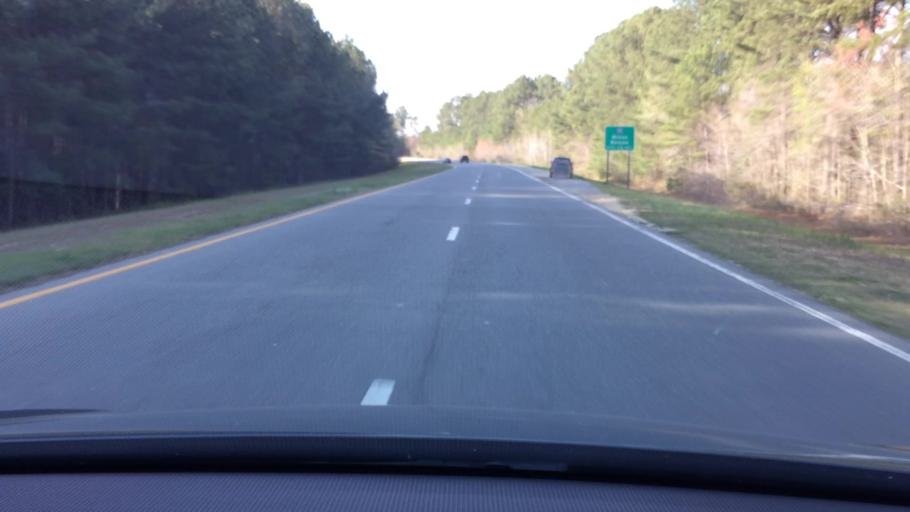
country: US
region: North Carolina
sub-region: Johnston County
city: Selma
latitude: 35.5116
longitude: -78.2819
